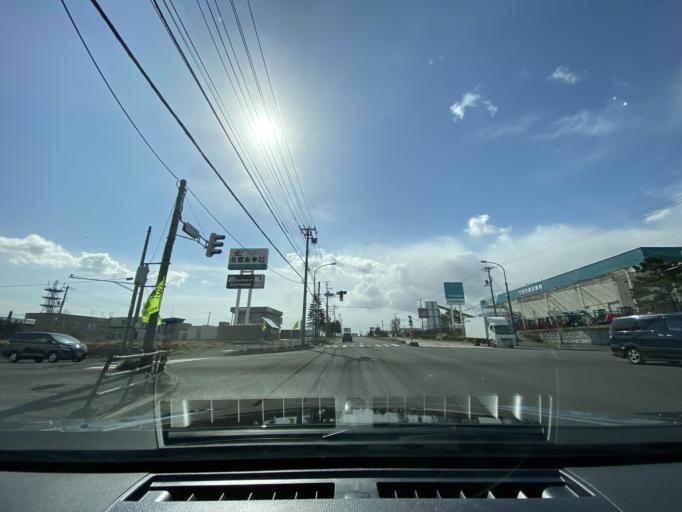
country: JP
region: Hokkaido
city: Kitahiroshima
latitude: 42.9636
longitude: 141.4886
